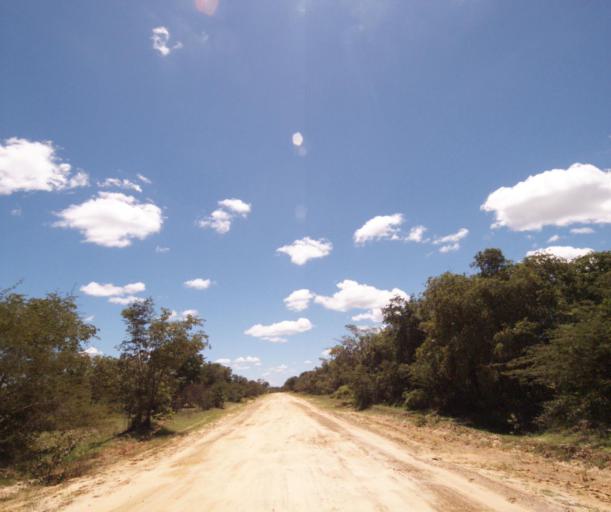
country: BR
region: Bahia
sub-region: Carinhanha
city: Carinhanha
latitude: -14.2079
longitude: -43.9734
